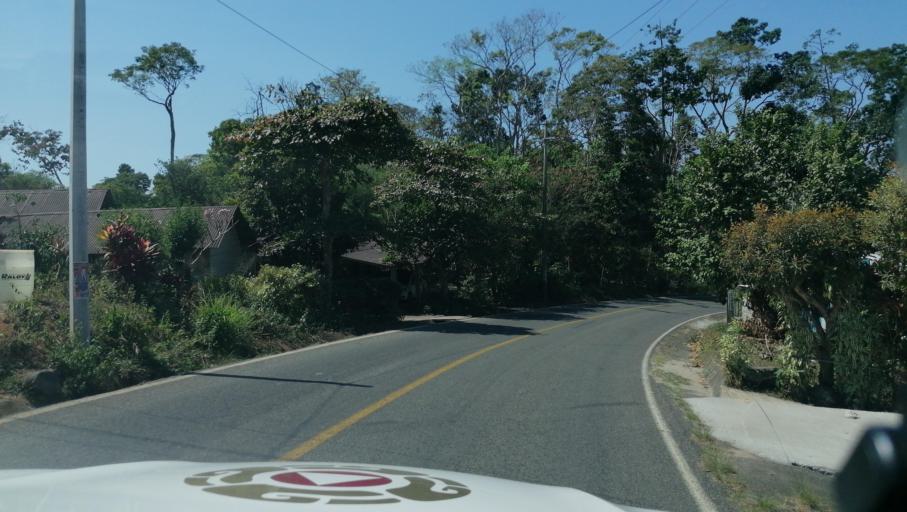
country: MX
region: Chiapas
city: Veinte de Noviembre
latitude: 14.9944
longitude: -92.2335
